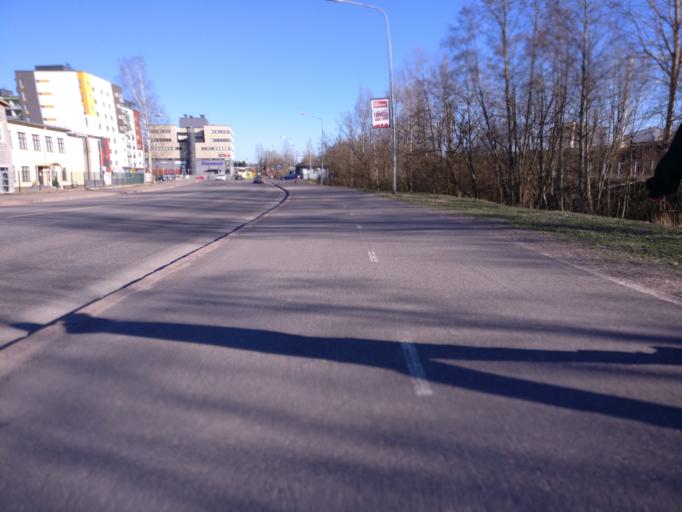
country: FI
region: Uusimaa
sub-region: Helsinki
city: Jaervenpaeae
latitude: 60.4772
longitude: 25.0860
